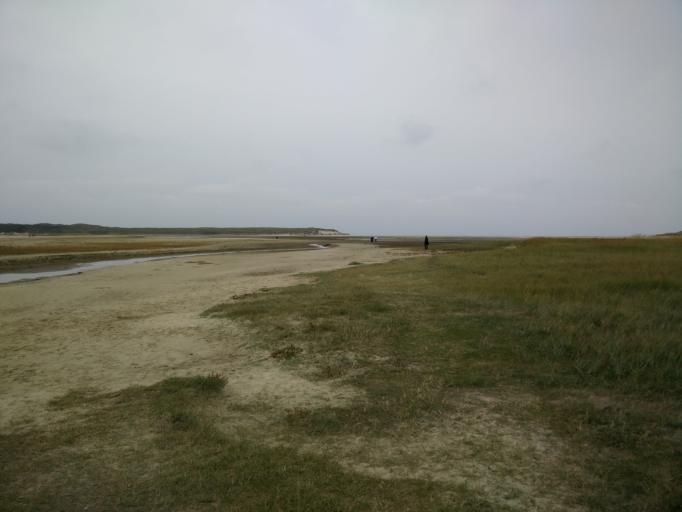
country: NL
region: North Holland
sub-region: Gemeente Texel
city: Den Burg
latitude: 53.1342
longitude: 4.8085
